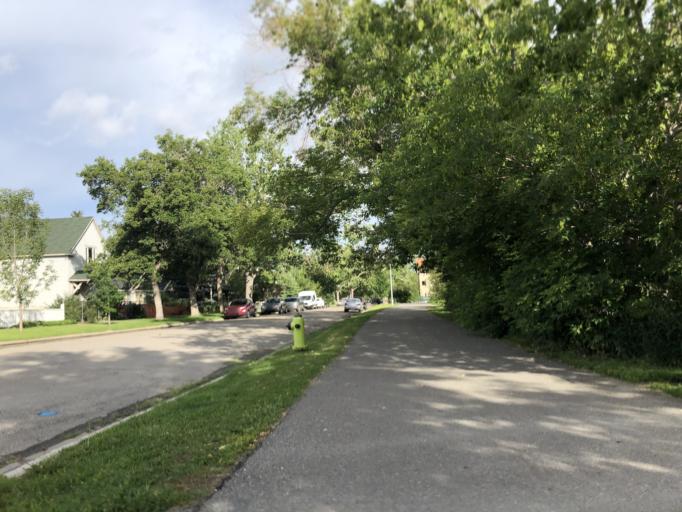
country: CA
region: Alberta
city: Calgary
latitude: 51.0334
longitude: -114.0131
